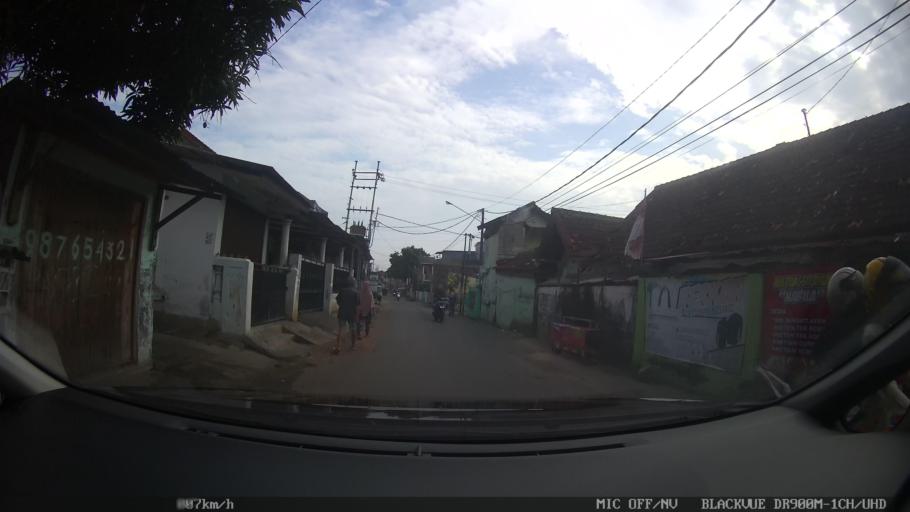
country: ID
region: Lampung
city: Bandarlampung
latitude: -5.4138
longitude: 105.2654
